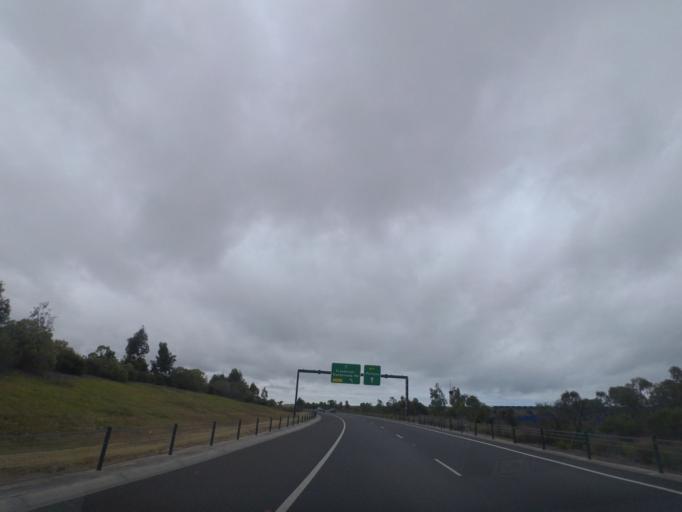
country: AU
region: Victoria
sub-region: Frankston
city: Carrum Downs
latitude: -38.0920
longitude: 145.1553
